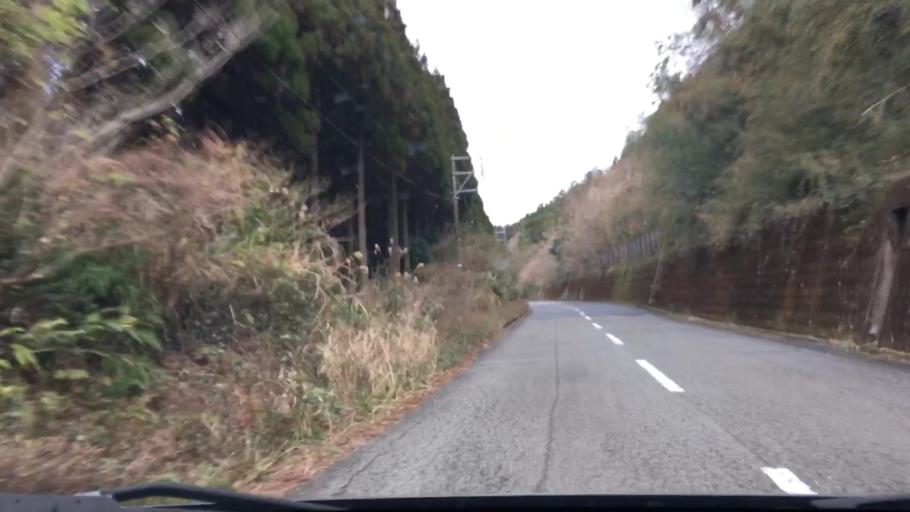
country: JP
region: Miyazaki
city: Nichinan
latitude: 31.6634
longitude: 131.3169
